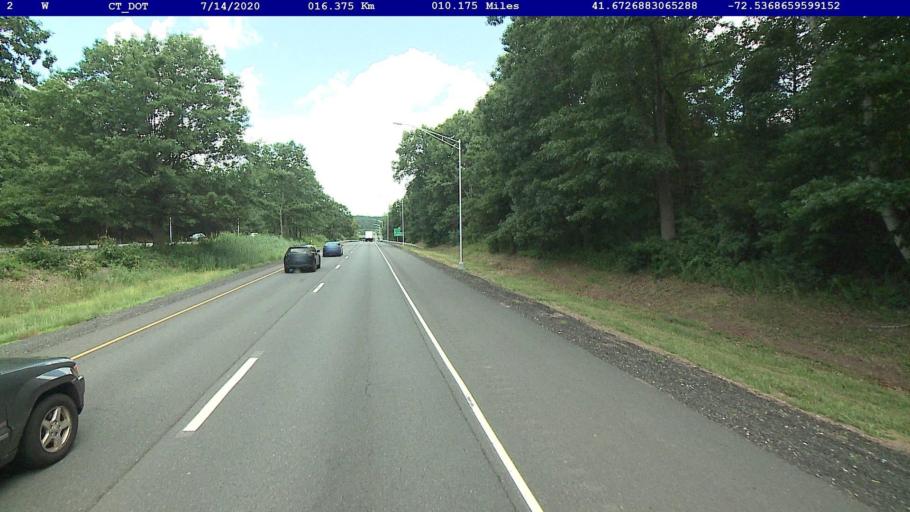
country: US
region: Connecticut
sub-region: Hartford County
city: Glastonbury Center
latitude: 41.6727
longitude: -72.5369
